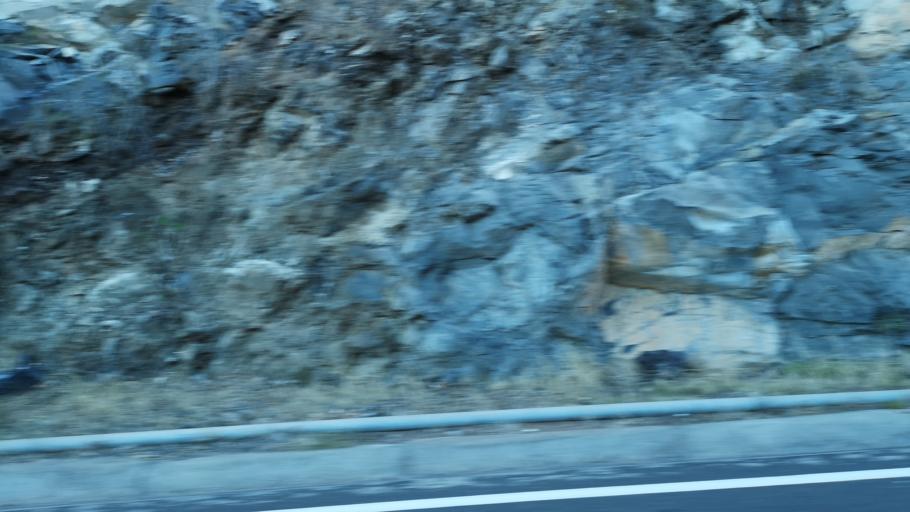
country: ES
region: Canary Islands
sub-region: Provincia de Santa Cruz de Tenerife
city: Alajero
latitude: 28.0309
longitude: -17.2031
